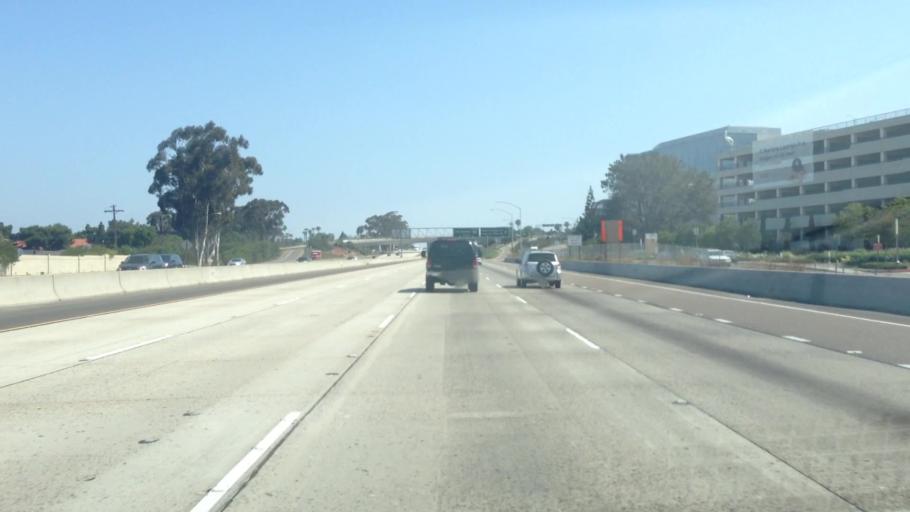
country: US
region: California
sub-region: San Diego County
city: San Diego
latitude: 32.7970
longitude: -117.1570
